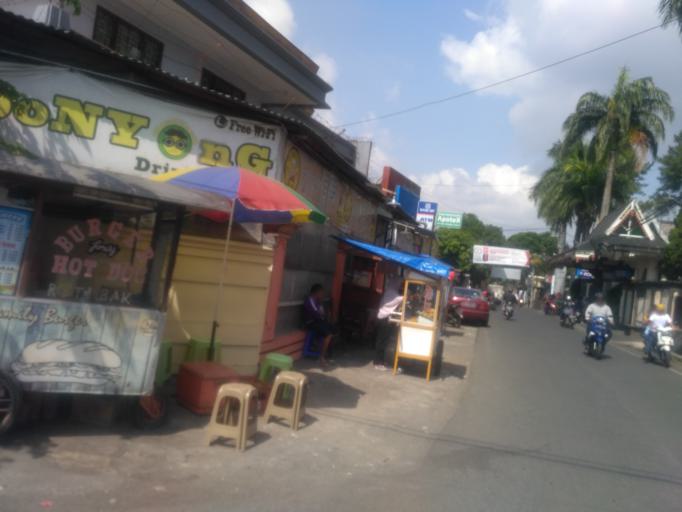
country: ID
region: East Java
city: Malang
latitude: -7.9417
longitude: 112.6382
